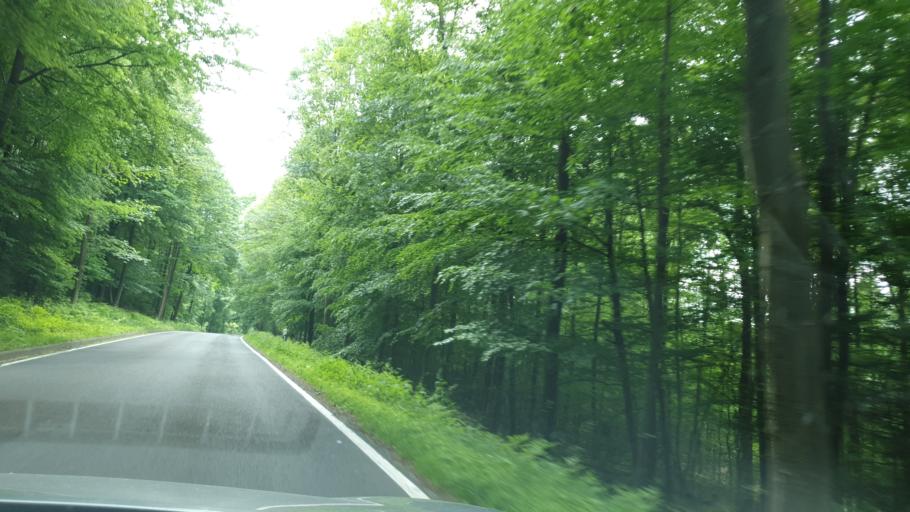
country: DE
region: Rheinland-Pfalz
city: Neuhausel
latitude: 50.3947
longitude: 7.7154
